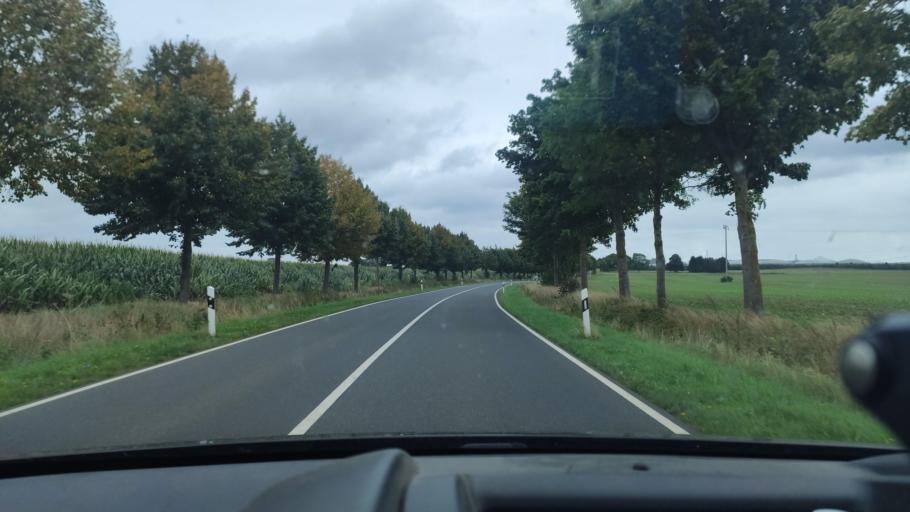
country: DE
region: Mecklenburg-Vorpommern
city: Guestrow
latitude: 53.8283
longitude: 12.1777
